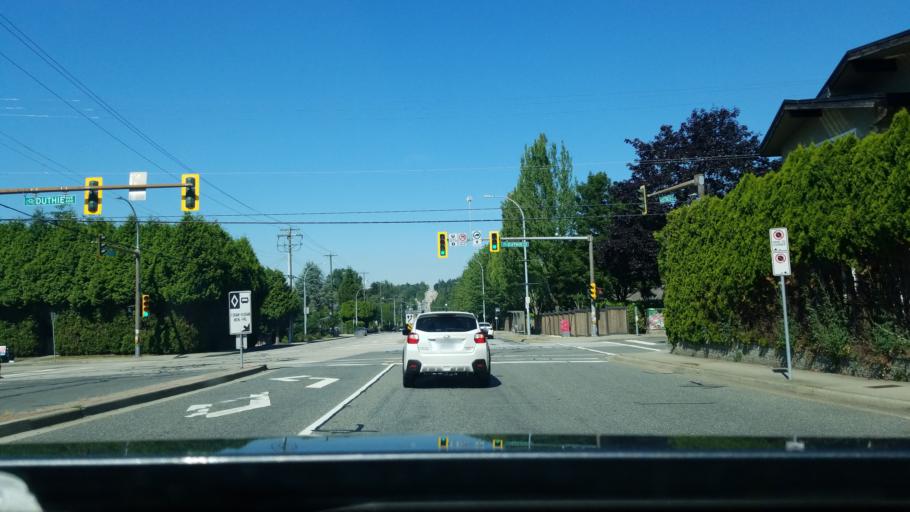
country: CA
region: British Columbia
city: Burnaby
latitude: 49.2804
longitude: -122.9529
